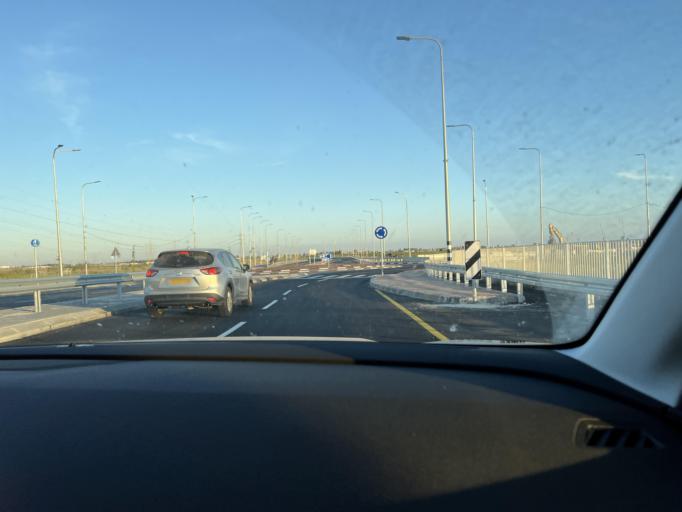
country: IL
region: Central District
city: Gan Yavne
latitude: 31.8143
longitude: 34.7046
